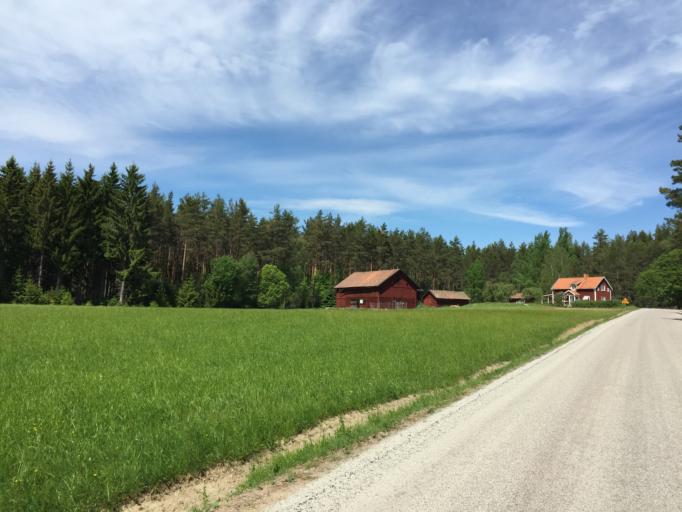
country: SE
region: Soedermanland
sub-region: Vingakers Kommun
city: Vingaker
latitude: 58.9784
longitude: 15.6811
